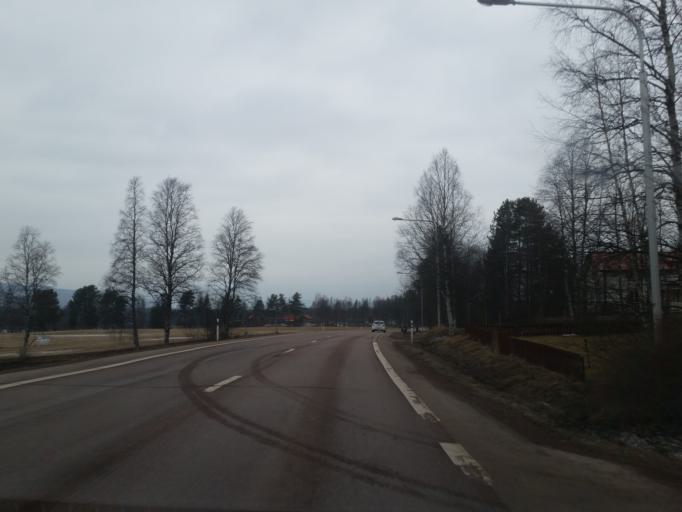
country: SE
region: Dalarna
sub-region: Alvdalens Kommun
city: AElvdalen
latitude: 61.2122
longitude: 14.0554
